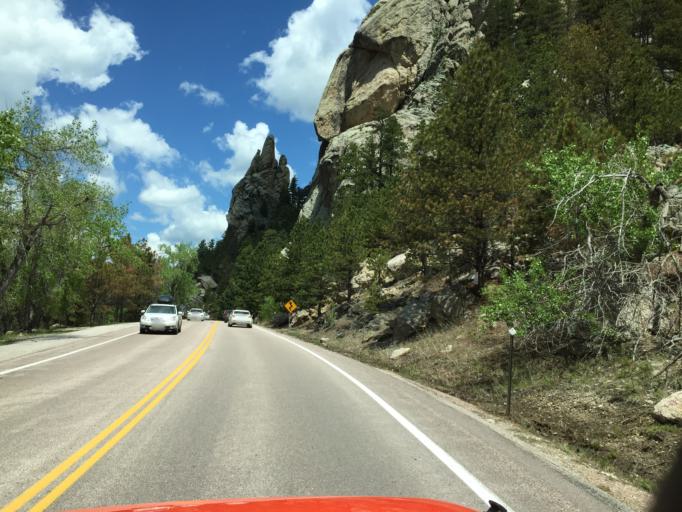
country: US
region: South Dakota
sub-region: Custer County
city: Custer
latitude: 43.8778
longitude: -103.4605
